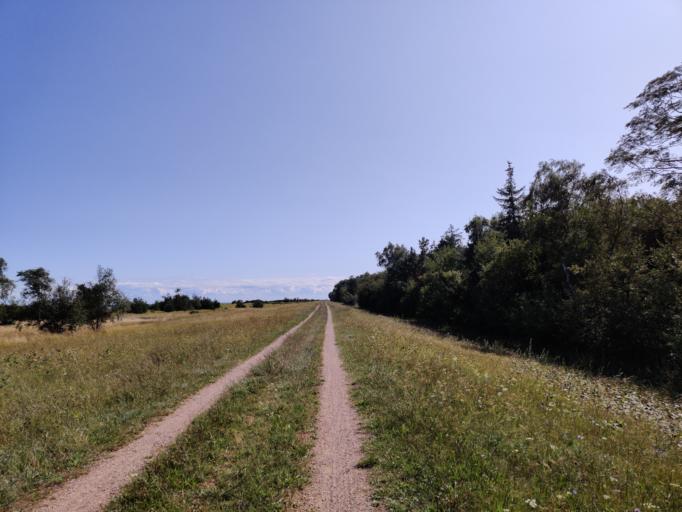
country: DK
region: Zealand
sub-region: Guldborgsund Kommune
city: Nykobing Falster
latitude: 54.6152
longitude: 11.9642
